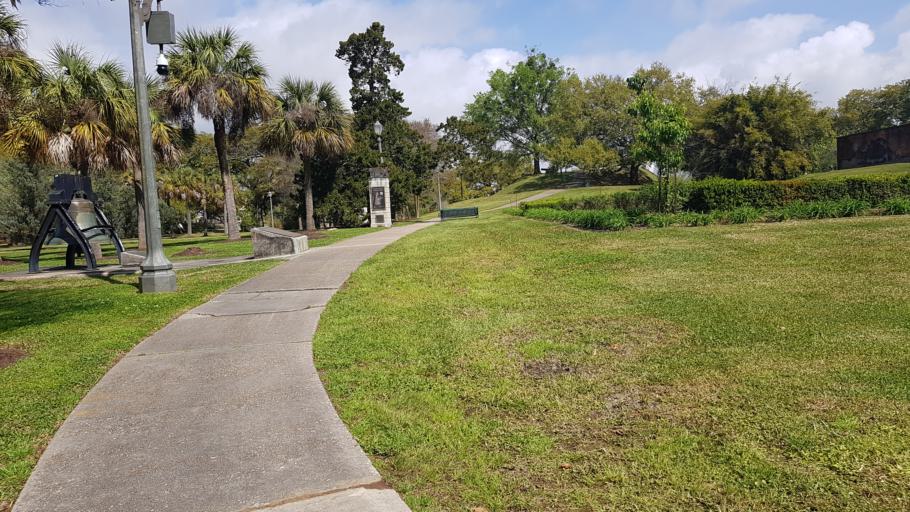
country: US
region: Louisiana
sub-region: West Baton Rouge Parish
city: Port Allen
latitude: 30.4573
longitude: -91.1851
